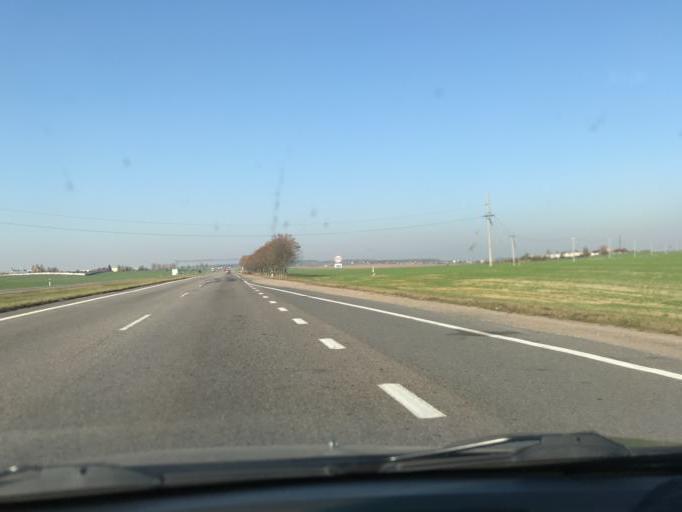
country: BY
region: Minsk
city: Luhavaya Slabada
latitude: 53.7365
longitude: 27.8472
